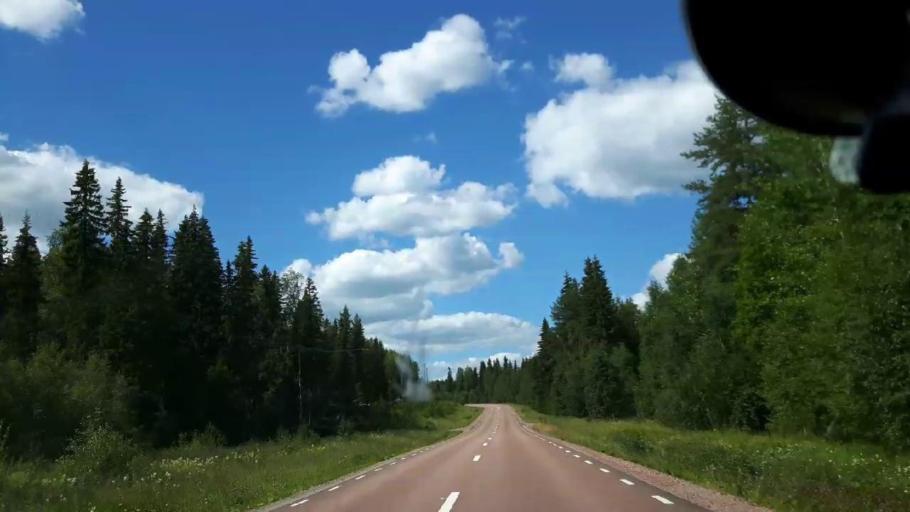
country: SE
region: Jaemtland
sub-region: Ragunda Kommun
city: Hammarstrand
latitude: 63.0166
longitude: 16.6156
